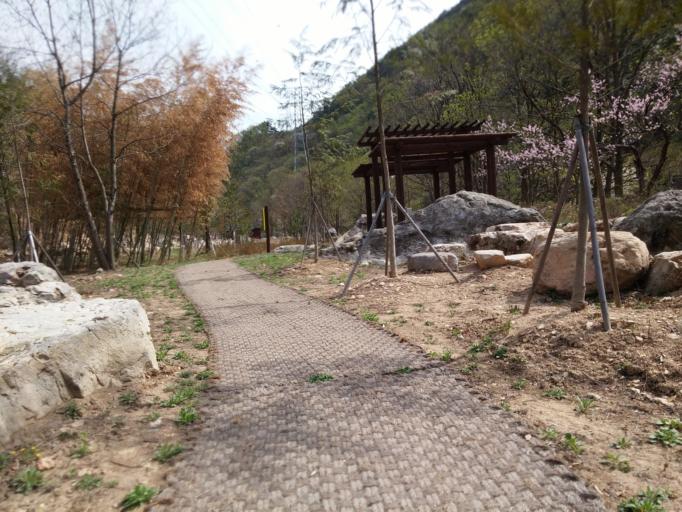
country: KR
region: Chungcheongbuk-do
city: Okcheon
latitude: 36.2391
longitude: 127.5566
